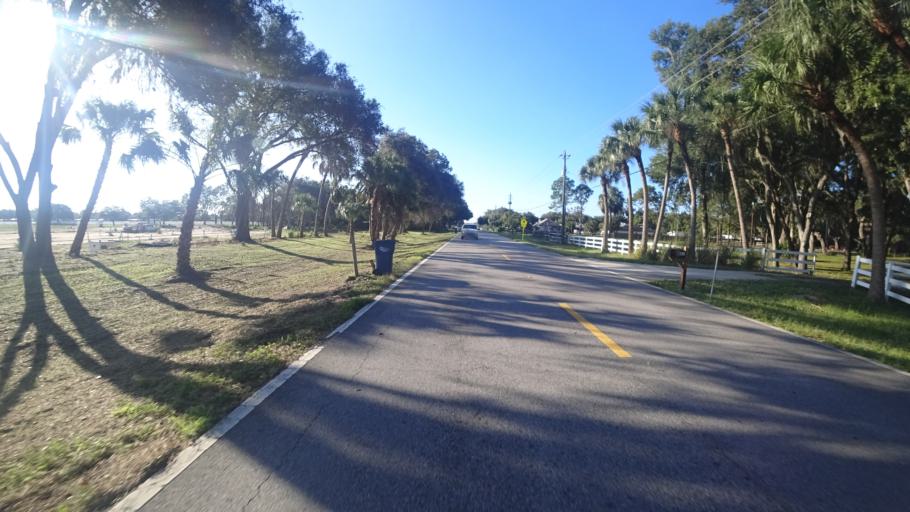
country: US
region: Florida
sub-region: Manatee County
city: Memphis
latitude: 27.5696
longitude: -82.5564
